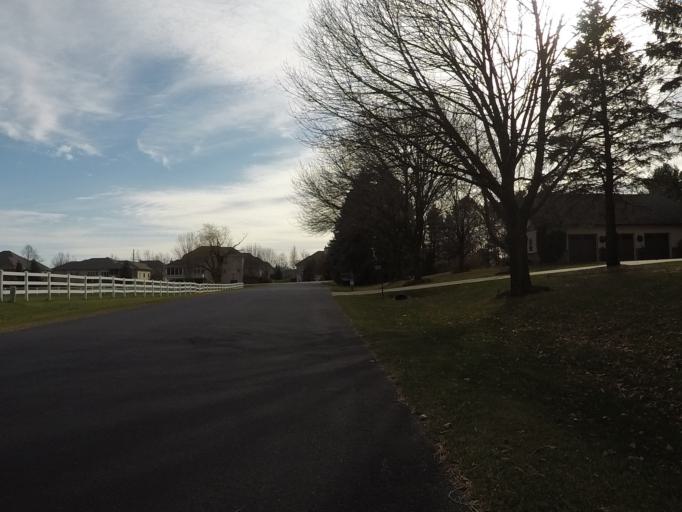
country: US
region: Wisconsin
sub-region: Dane County
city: Middleton
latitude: 43.0831
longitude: -89.5586
